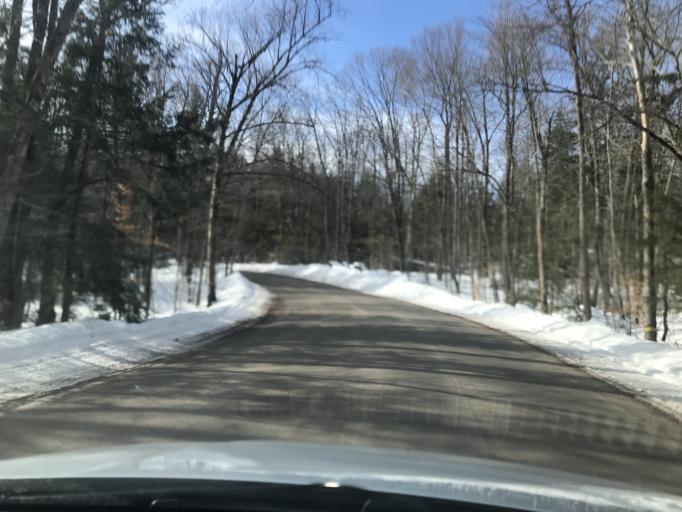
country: US
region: Wisconsin
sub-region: Menominee County
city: Legend Lake
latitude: 45.1235
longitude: -88.4263
